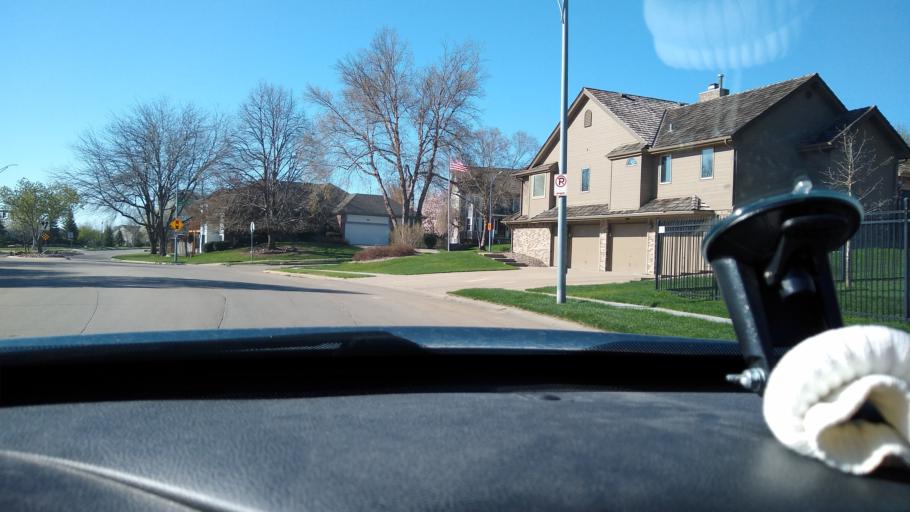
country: US
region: Nebraska
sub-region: Douglas County
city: Ralston
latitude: 41.1920
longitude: -96.0723
